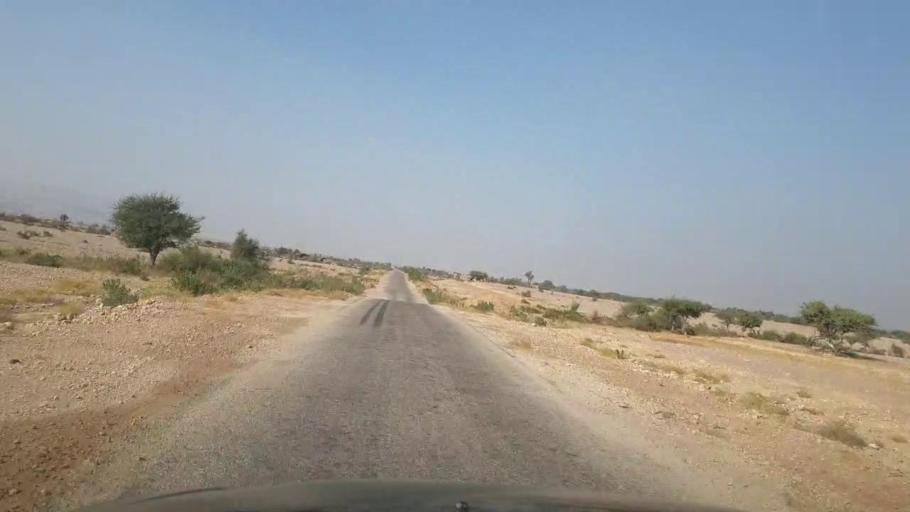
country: PK
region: Sindh
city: Jamshoro
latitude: 25.5817
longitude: 67.8211
